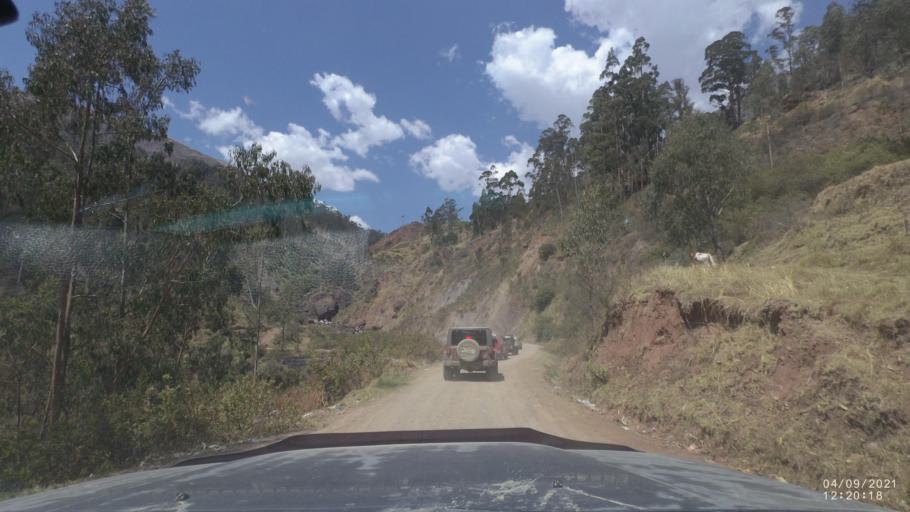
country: BO
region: Cochabamba
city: Colchani
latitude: -17.2398
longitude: -66.5276
